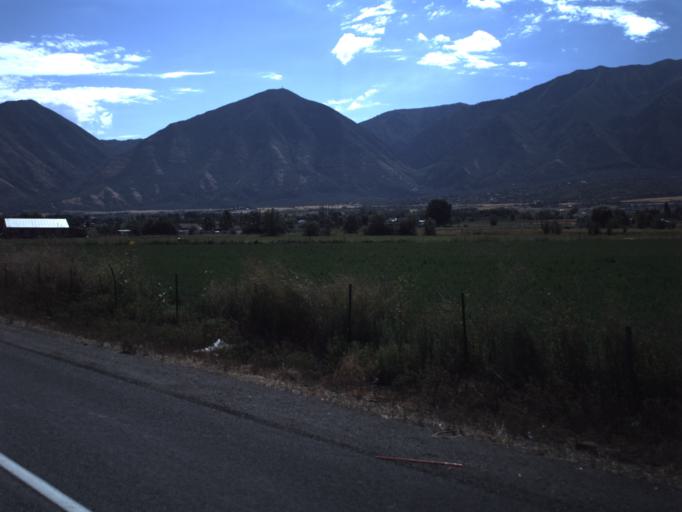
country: US
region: Utah
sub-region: Utah County
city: Payson
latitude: 40.0465
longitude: -111.7039
